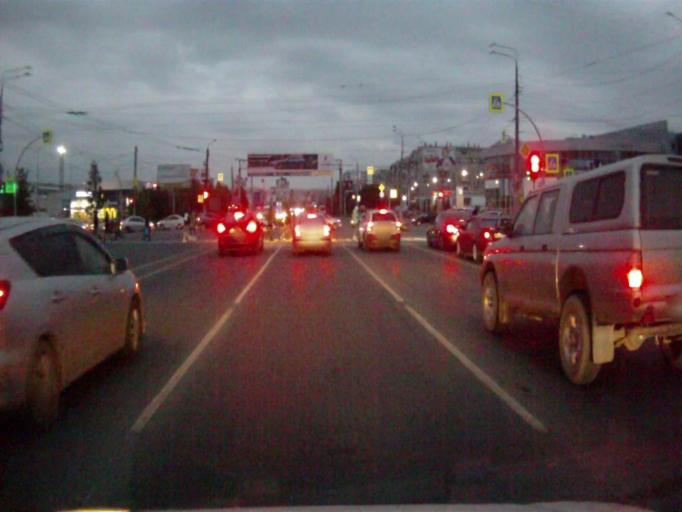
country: RU
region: Chelyabinsk
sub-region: Gorod Chelyabinsk
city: Chelyabinsk
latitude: 55.1738
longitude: 61.3051
